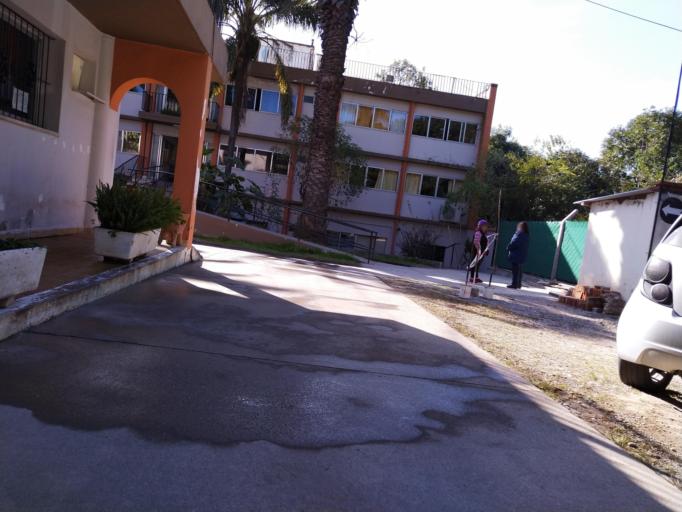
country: AR
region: Jujuy
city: San Salvador de Jujuy
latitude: -24.1783
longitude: -65.3446
